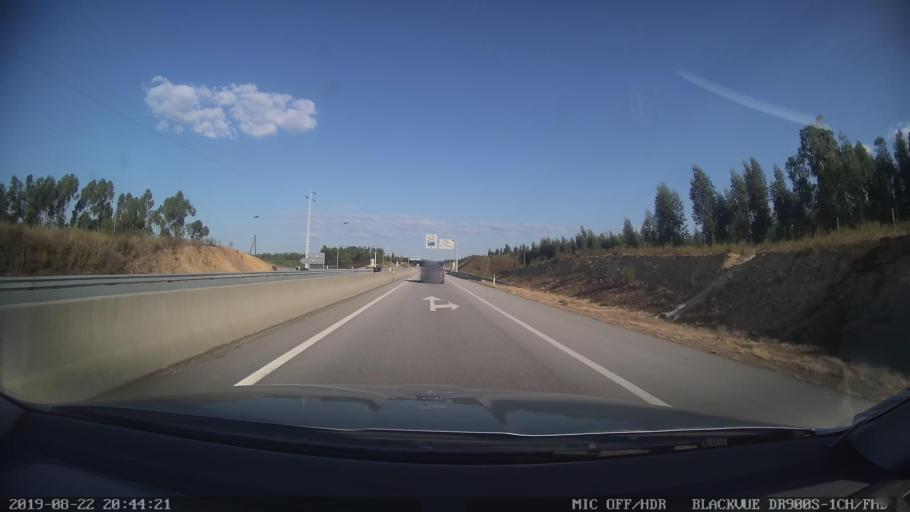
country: PT
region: Castelo Branco
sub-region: Proenca-A-Nova
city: Proenca-a-Nova
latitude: 39.7066
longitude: -7.8498
